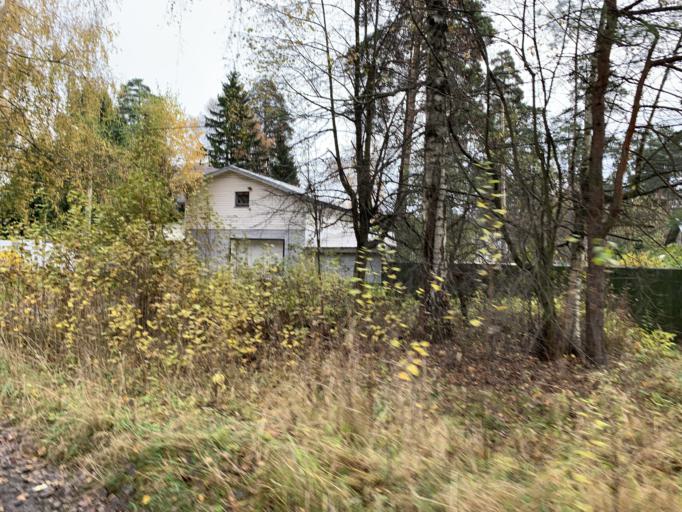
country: RU
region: Moskovskaya
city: Mamontovka
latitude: 55.9844
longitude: 37.8399
